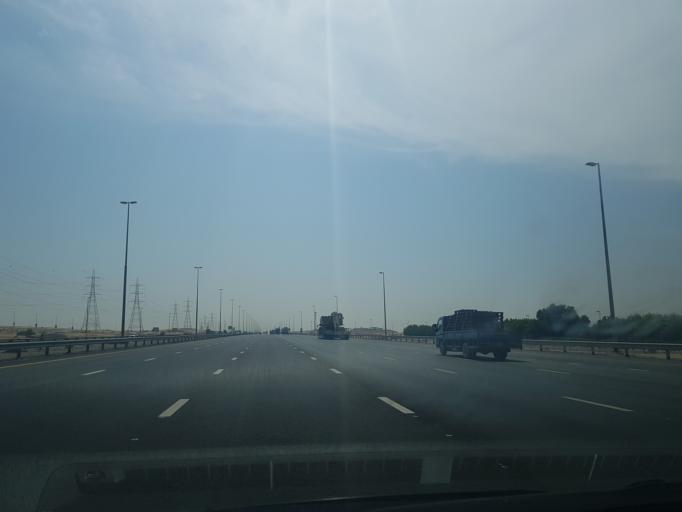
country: AE
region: Ash Shariqah
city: Sharjah
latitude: 25.2646
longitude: 55.5782
